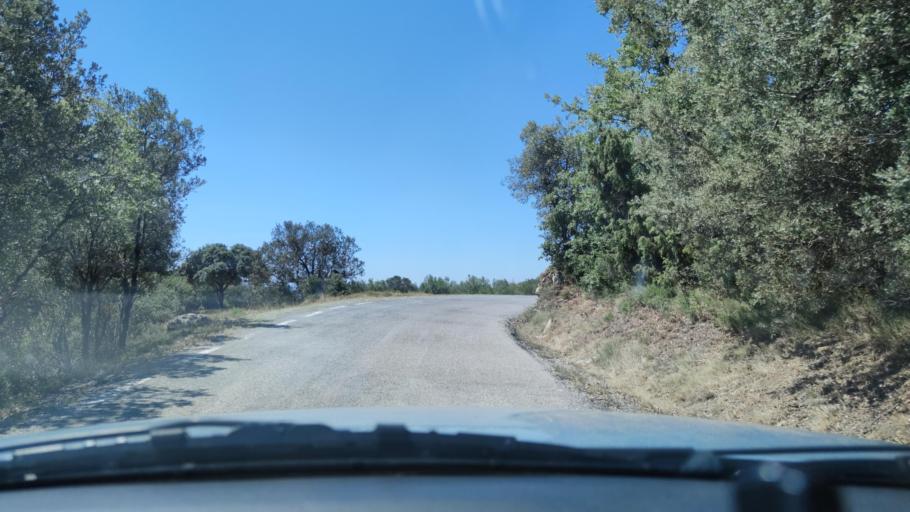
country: ES
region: Catalonia
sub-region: Provincia de Lleida
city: Tora de Riubregos
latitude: 41.8793
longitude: 1.4407
